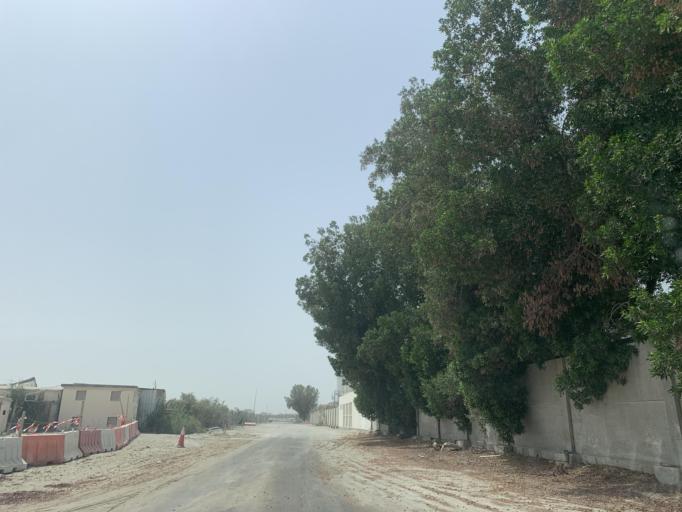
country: BH
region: Northern
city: Madinat `Isa
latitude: 26.1924
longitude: 50.5291
